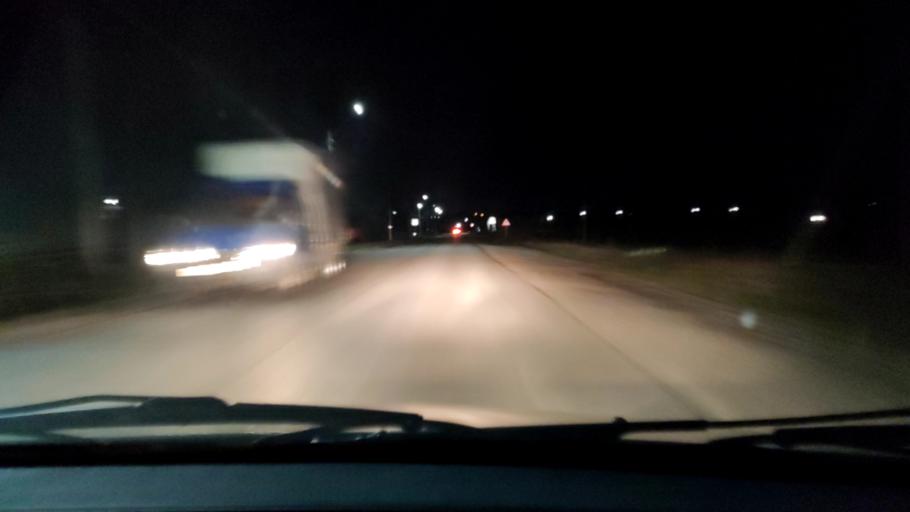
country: RU
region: Voronezj
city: Novaya Usman'
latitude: 51.6562
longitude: 39.4398
